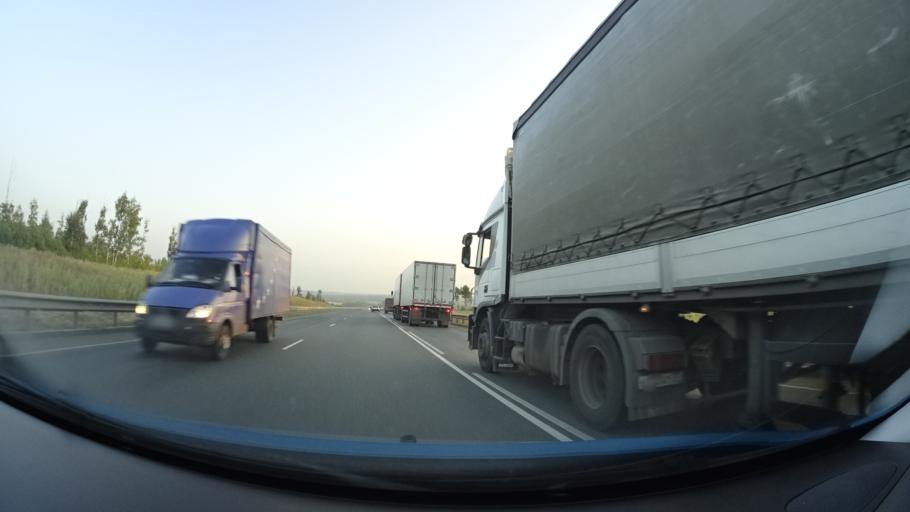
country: RU
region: Samara
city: Sernovodsk
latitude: 53.9041
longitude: 51.2836
